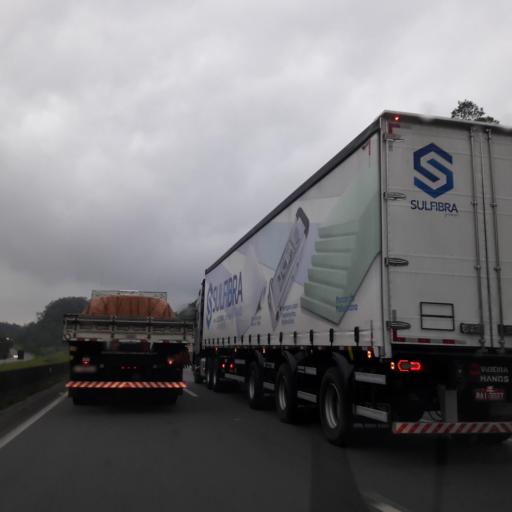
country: BR
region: Parana
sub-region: Antonina
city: Antonina
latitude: -25.0974
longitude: -48.6708
